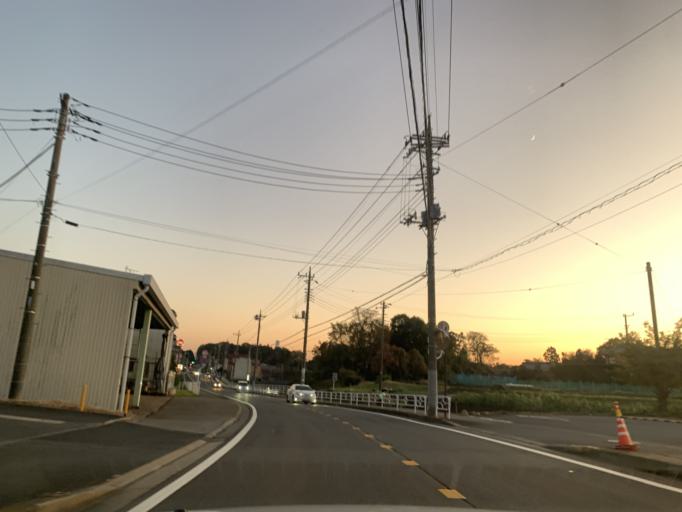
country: JP
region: Chiba
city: Nagareyama
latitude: 35.8940
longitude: 139.9005
